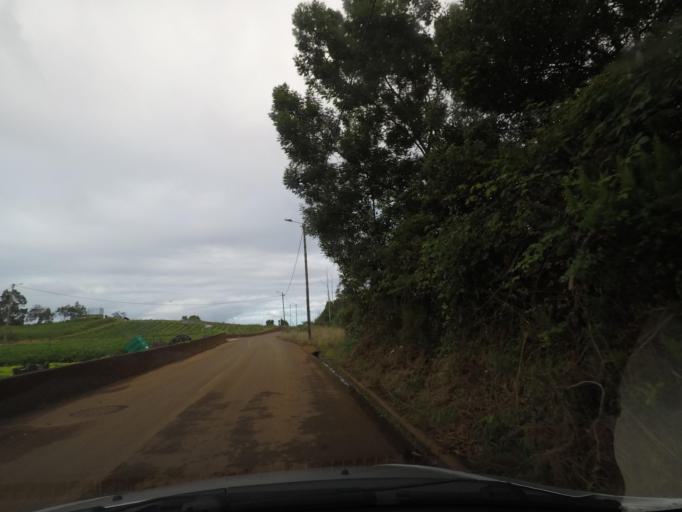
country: PT
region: Madeira
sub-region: Santana
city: Santana
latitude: 32.7802
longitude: -16.8780
